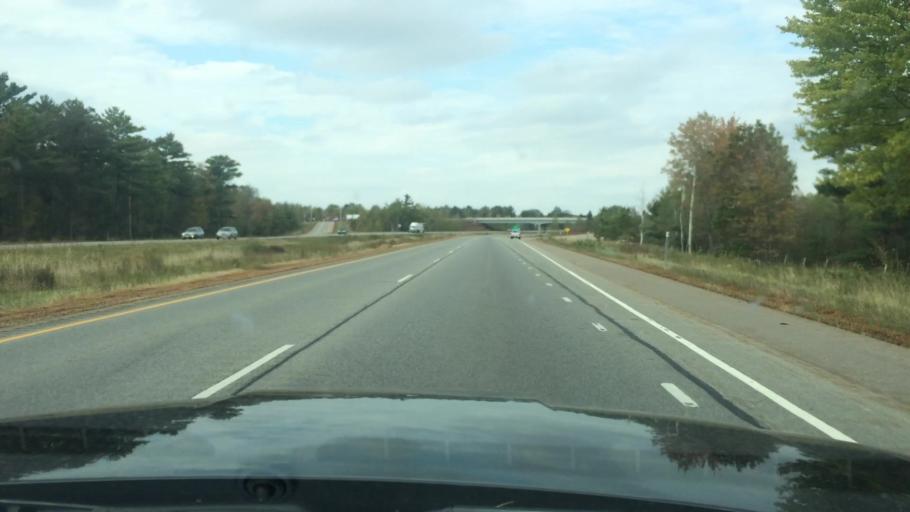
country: US
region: Wisconsin
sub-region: Marathon County
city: Mosinee
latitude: 44.7255
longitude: -89.6742
